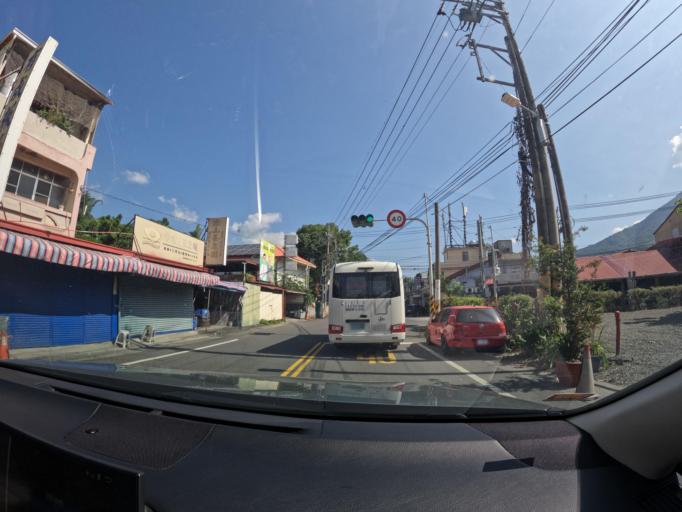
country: TW
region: Taiwan
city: Yujing
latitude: 23.0724
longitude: 120.6725
